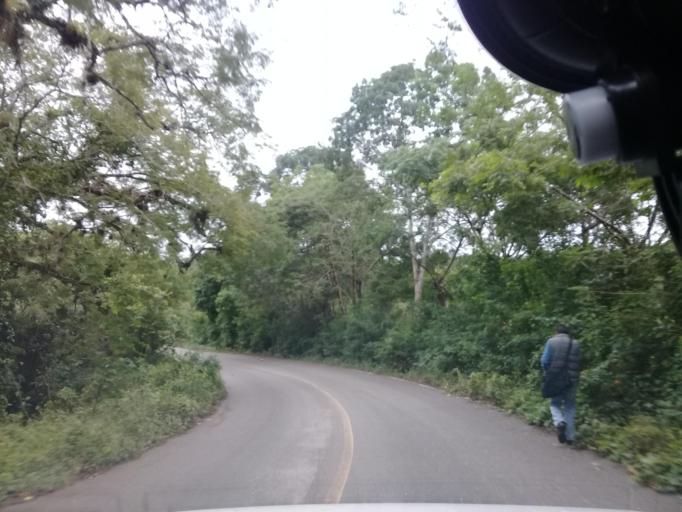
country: MX
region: Veracruz
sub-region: Chalma
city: San Pedro Coyutla
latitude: 21.2082
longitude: -98.4066
